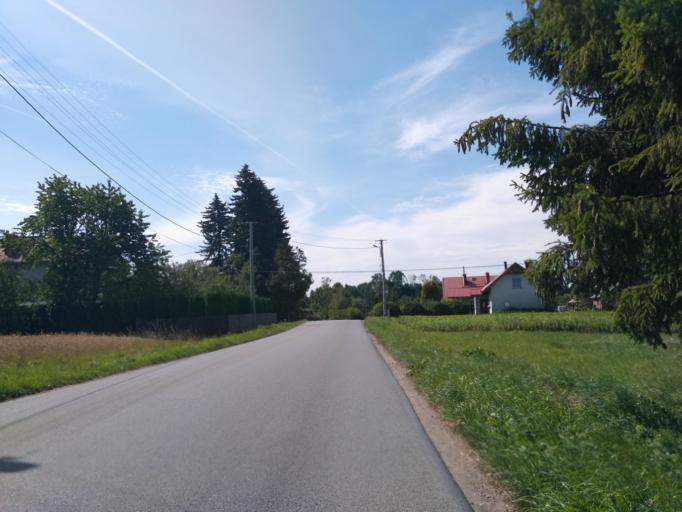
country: PL
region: Subcarpathian Voivodeship
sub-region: Powiat krosnienski
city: Korczyna
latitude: 49.7095
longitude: 21.8280
